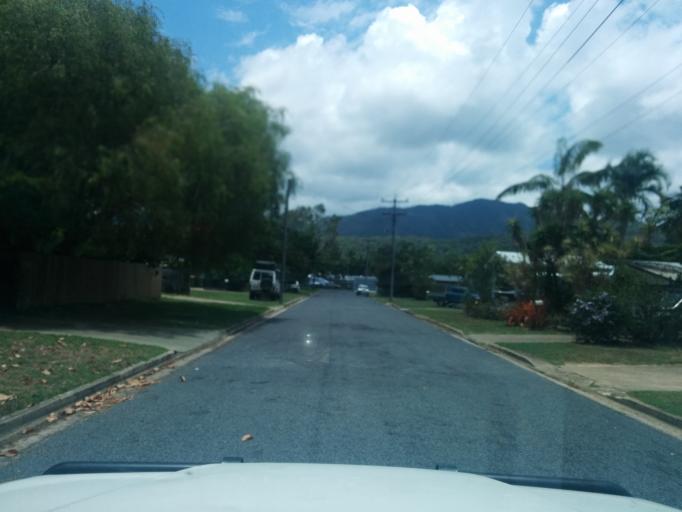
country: AU
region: Queensland
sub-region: Cairns
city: Trinity Beach
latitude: -16.8029
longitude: 145.7013
